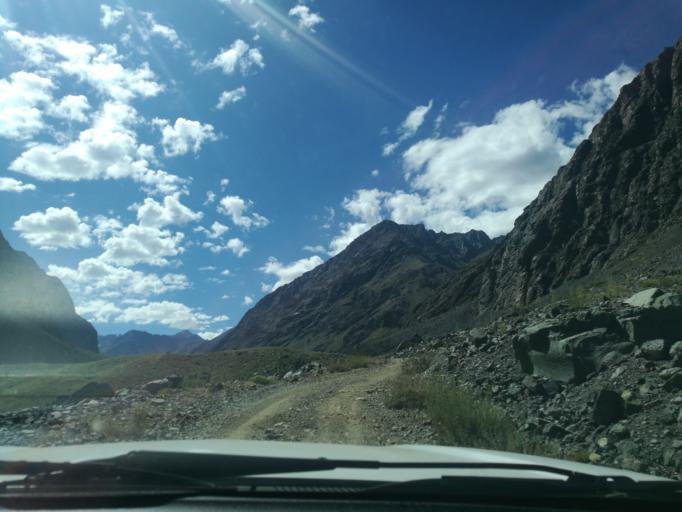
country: CL
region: O'Higgins
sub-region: Provincia de Cachapoal
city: Machali
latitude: -34.4072
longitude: -70.2442
